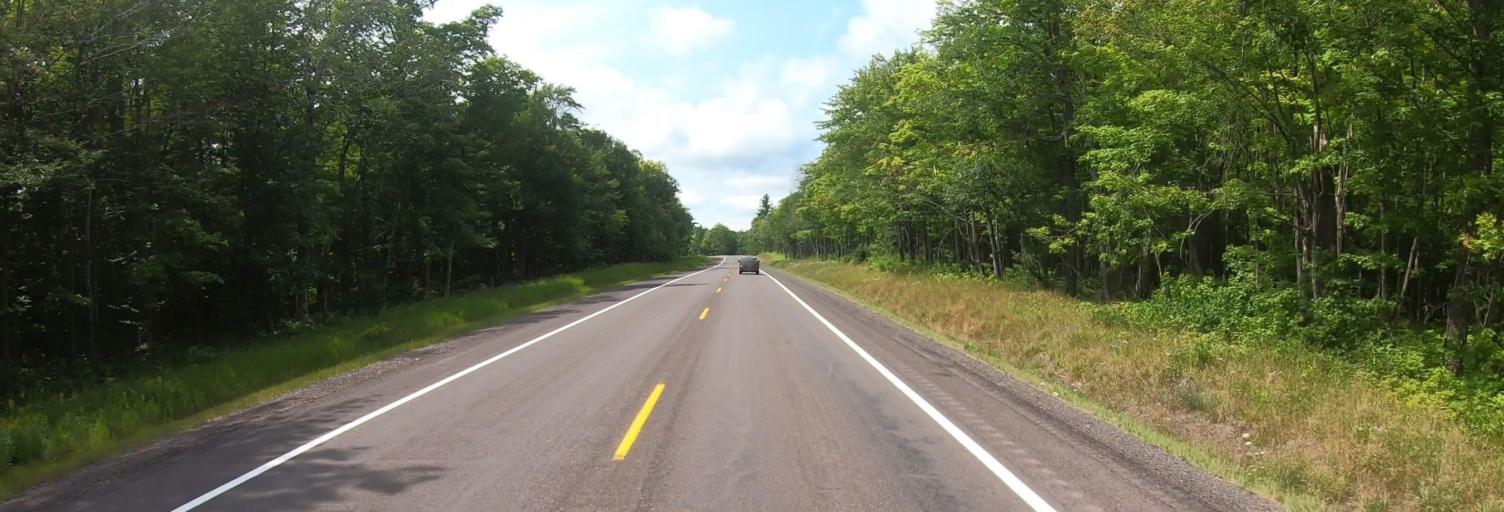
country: US
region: Michigan
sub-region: Houghton County
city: Hancock
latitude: 47.0299
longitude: -88.7082
